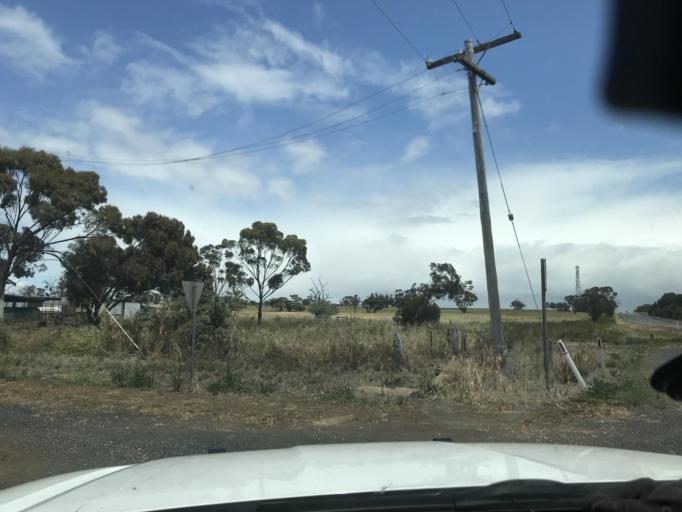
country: AU
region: South Australia
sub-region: Tatiara
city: Bordertown
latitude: -36.3618
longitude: 141.1242
